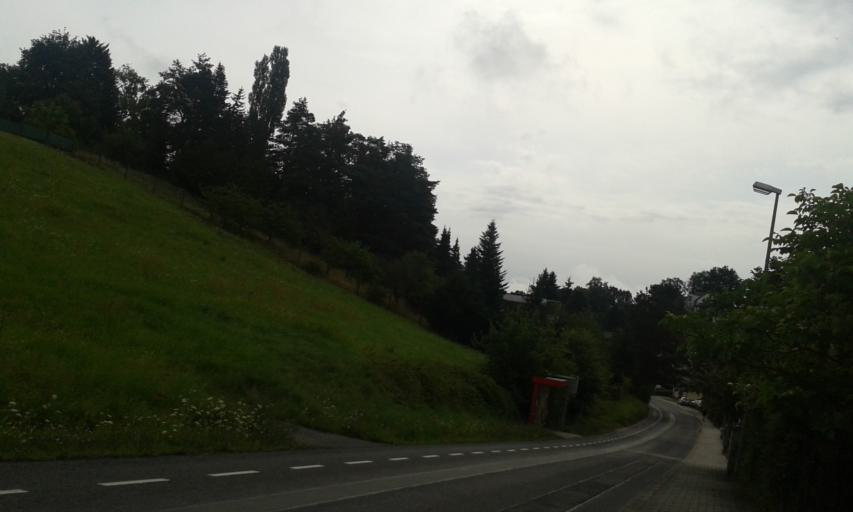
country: DE
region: Bavaria
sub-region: Upper Franconia
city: Bamberg
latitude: 49.8702
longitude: 10.8947
